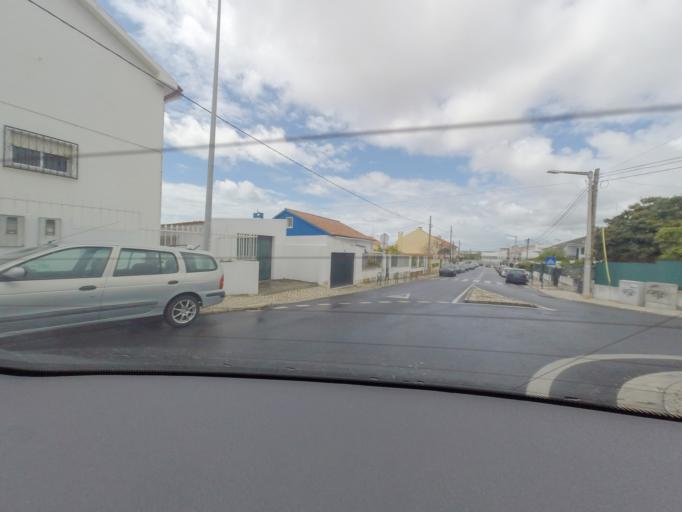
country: PT
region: Lisbon
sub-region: Cascais
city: Parede
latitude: 38.7109
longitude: -9.3623
